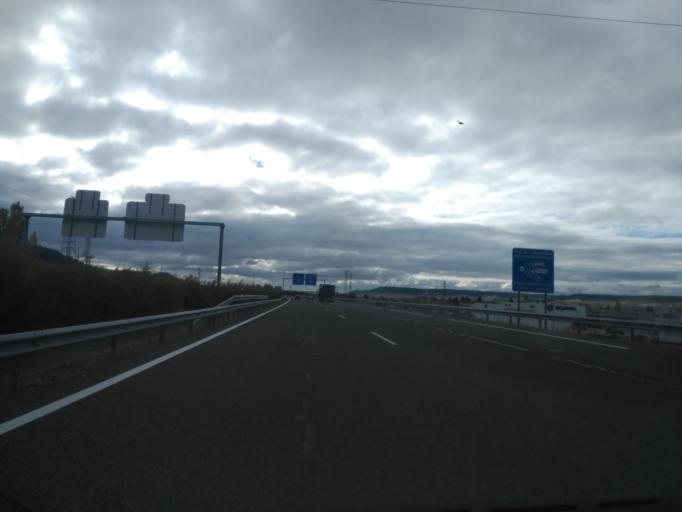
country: ES
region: Castille and Leon
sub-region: Provincia de Palencia
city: Palencia
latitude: 41.9998
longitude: -4.5023
